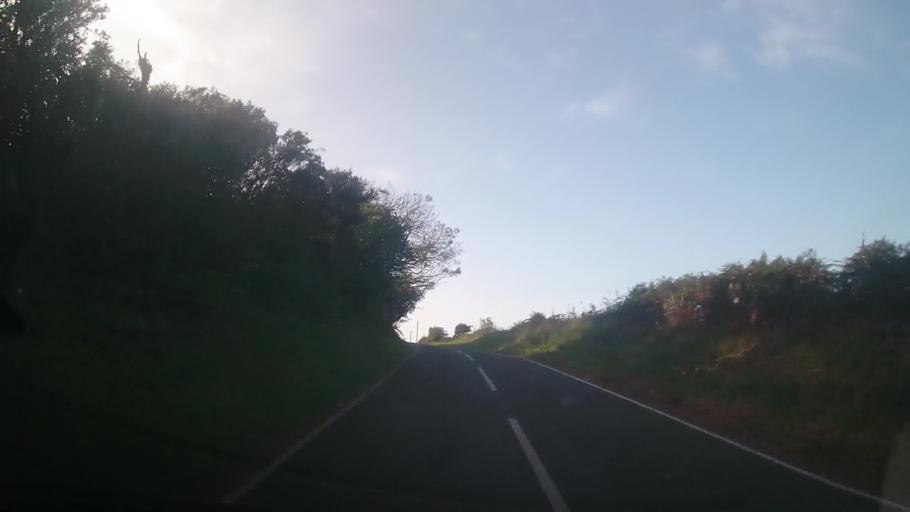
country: GB
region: Wales
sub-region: Pembrokeshire
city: Ambleston
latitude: 51.9640
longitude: -4.8967
